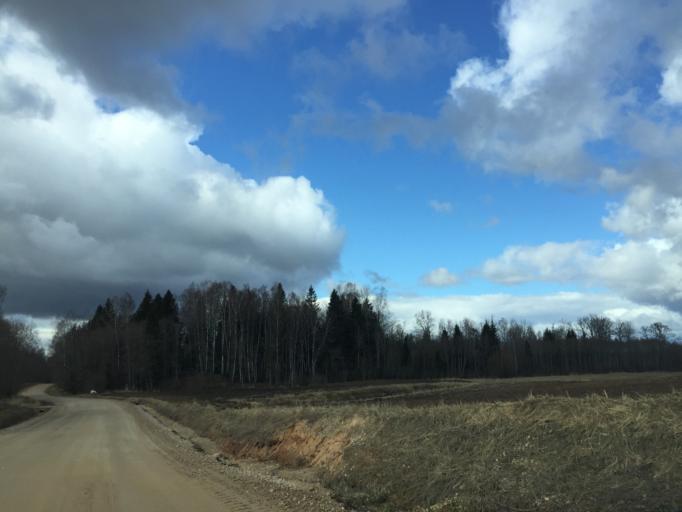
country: LV
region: Akniste
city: Akniste
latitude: 56.1104
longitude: 25.8771
